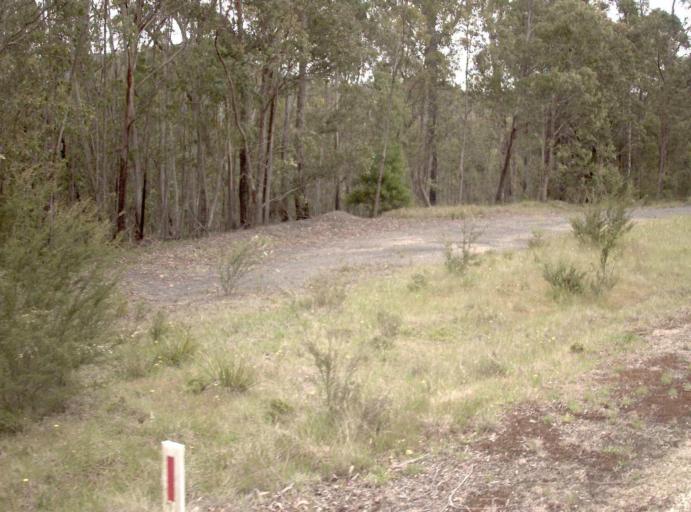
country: AU
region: New South Wales
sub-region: Bombala
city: Bombala
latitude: -37.2788
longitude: 149.2237
